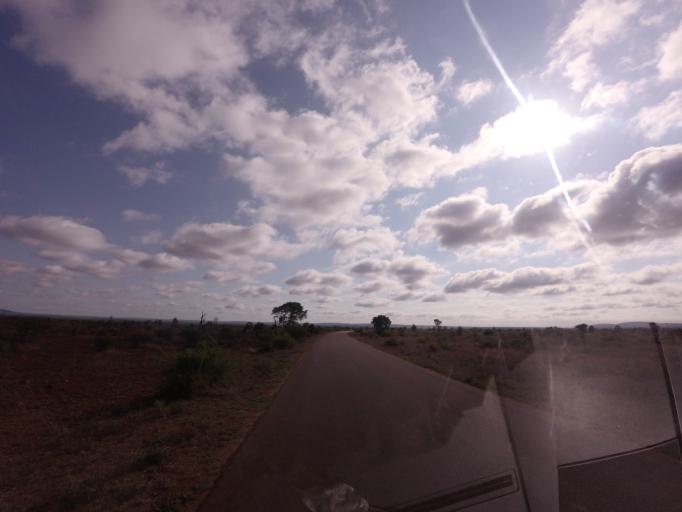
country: ZA
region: Mpumalanga
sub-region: Ehlanzeni District
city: Komatipoort
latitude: -25.1798
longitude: 31.9043
